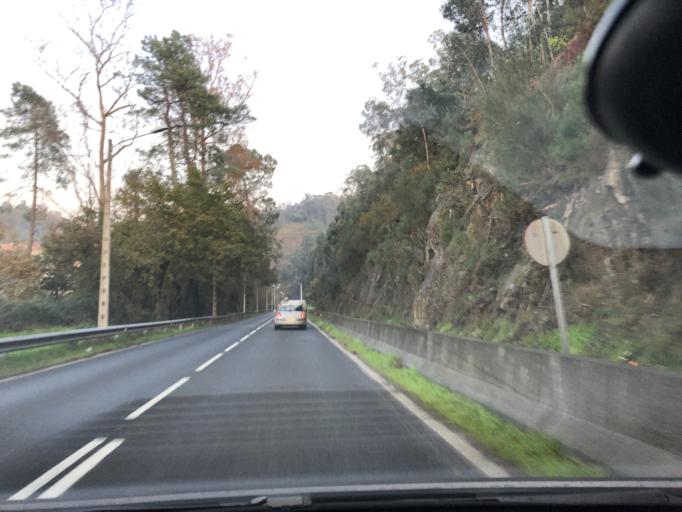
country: ES
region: Galicia
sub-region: Provincia de Pontevedra
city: Marin
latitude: 42.3823
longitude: -8.7209
